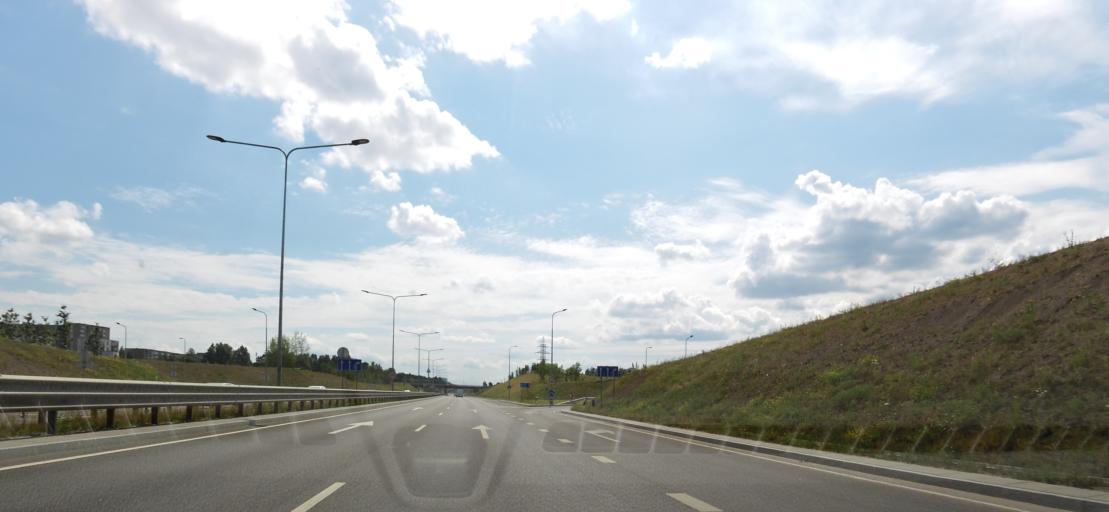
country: LT
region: Vilnius County
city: Justiniskes
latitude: 54.7245
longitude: 25.2077
